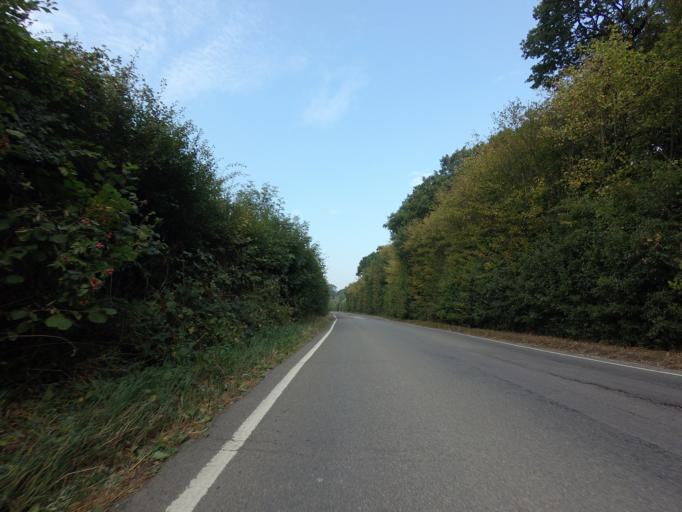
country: GB
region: England
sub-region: Kent
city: Ashford
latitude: 51.1080
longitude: 0.7834
